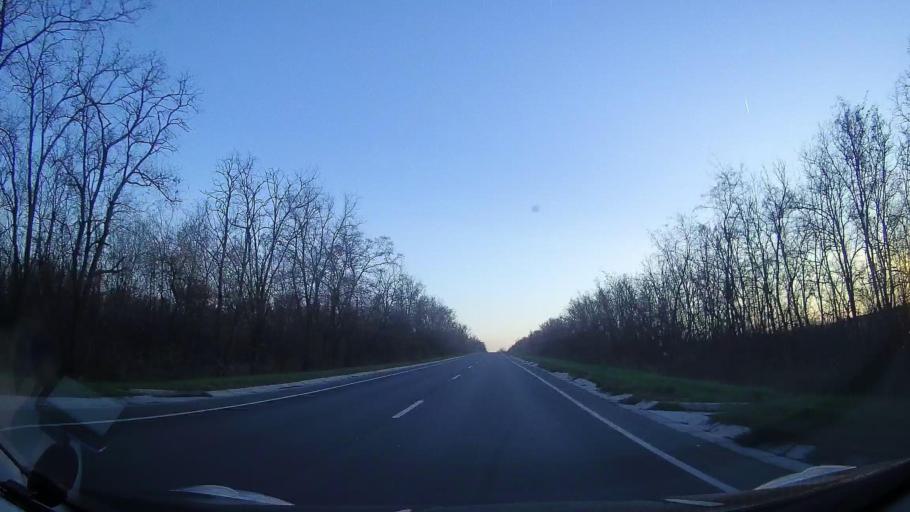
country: RU
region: Rostov
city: Bagayevskaya
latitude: 47.1074
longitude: 40.2767
